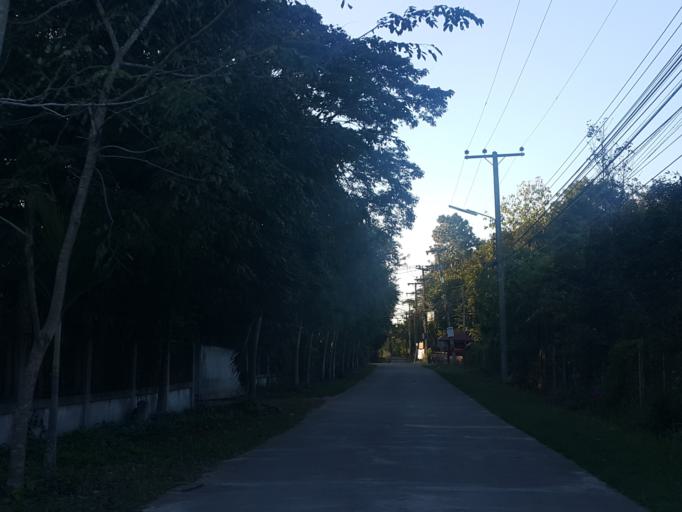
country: TH
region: Chiang Mai
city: San Sai
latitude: 18.8746
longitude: 99.1517
